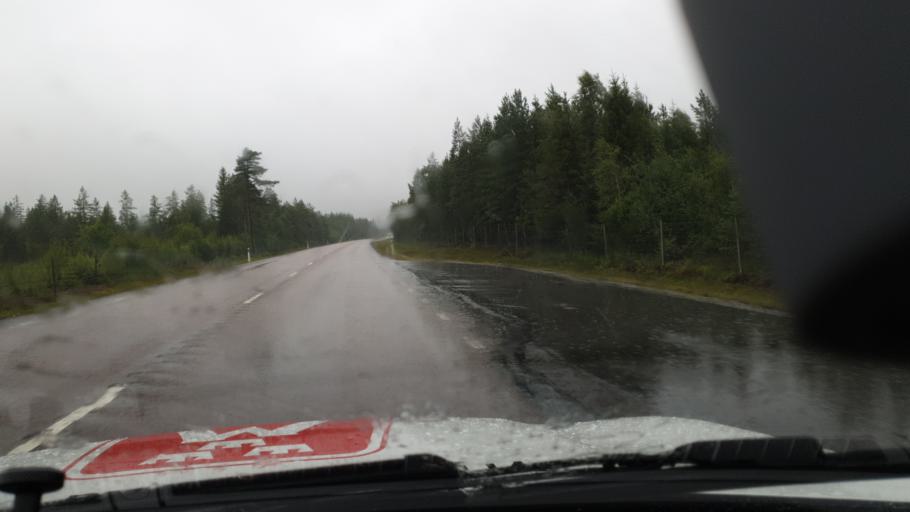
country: SE
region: Vaesterbotten
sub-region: Skelleftea Kommun
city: Burea
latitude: 64.4176
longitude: 21.2890
